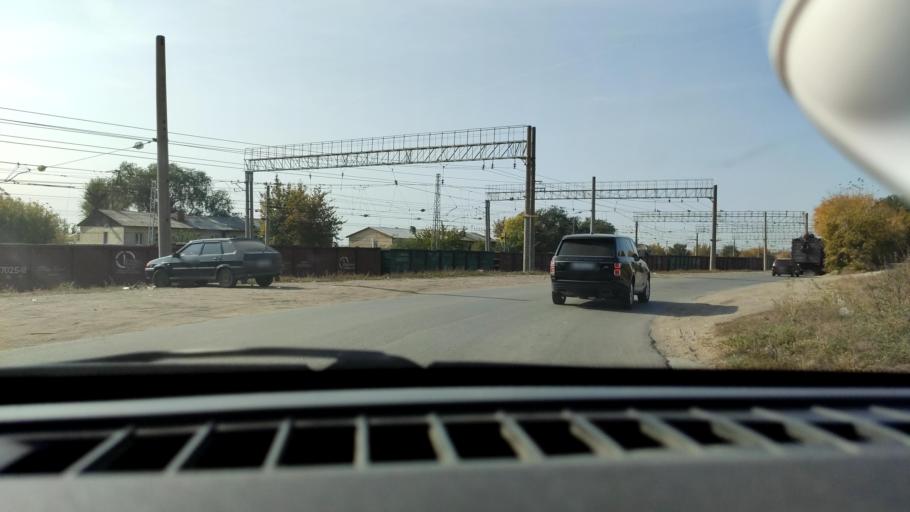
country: RU
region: Samara
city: Samara
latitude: 53.1763
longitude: 50.1540
